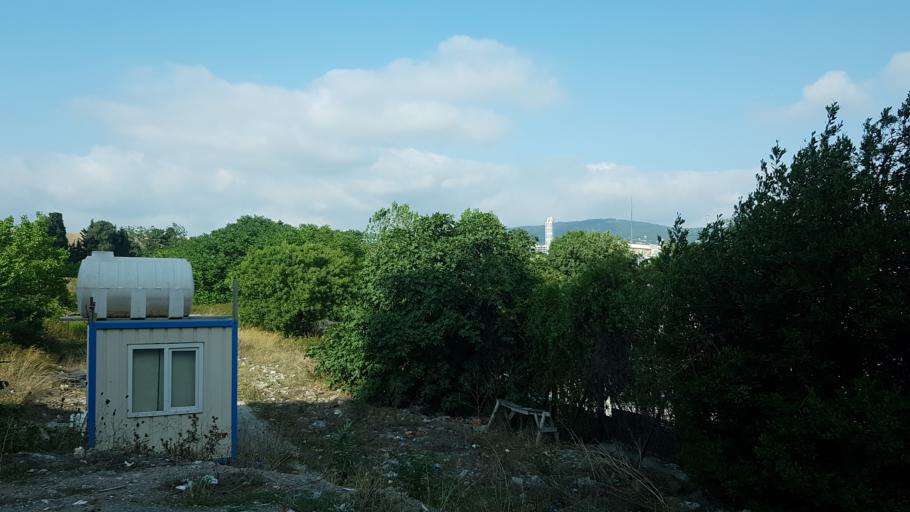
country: TR
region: Istanbul
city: Maltepe
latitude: 40.9003
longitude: 29.2009
